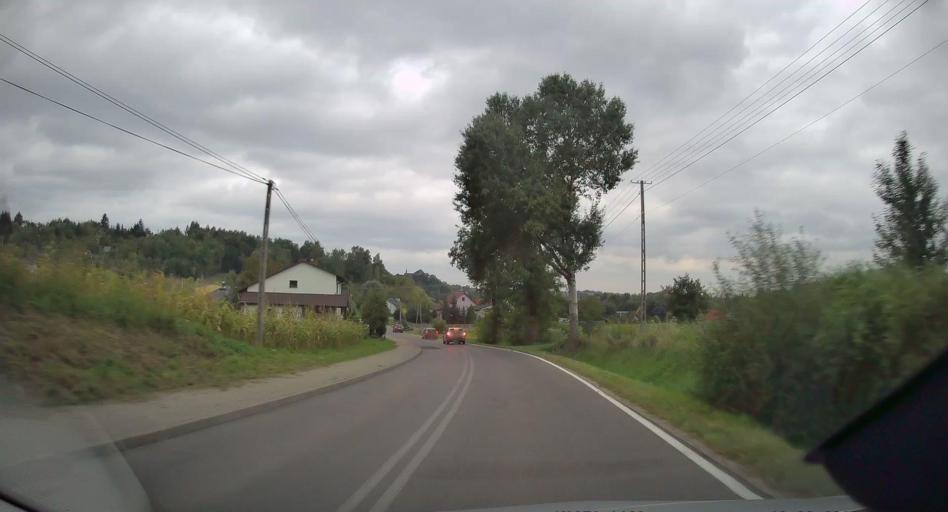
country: PL
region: Lesser Poland Voivodeship
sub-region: Powiat krakowski
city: Slomniki
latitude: 50.1547
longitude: 20.1047
